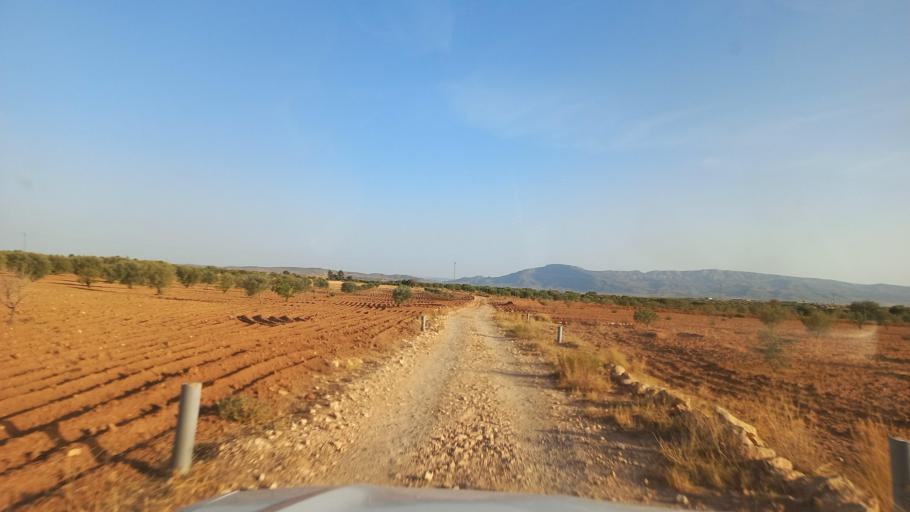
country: TN
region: Al Qasrayn
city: Kasserine
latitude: 35.2594
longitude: 8.9060
